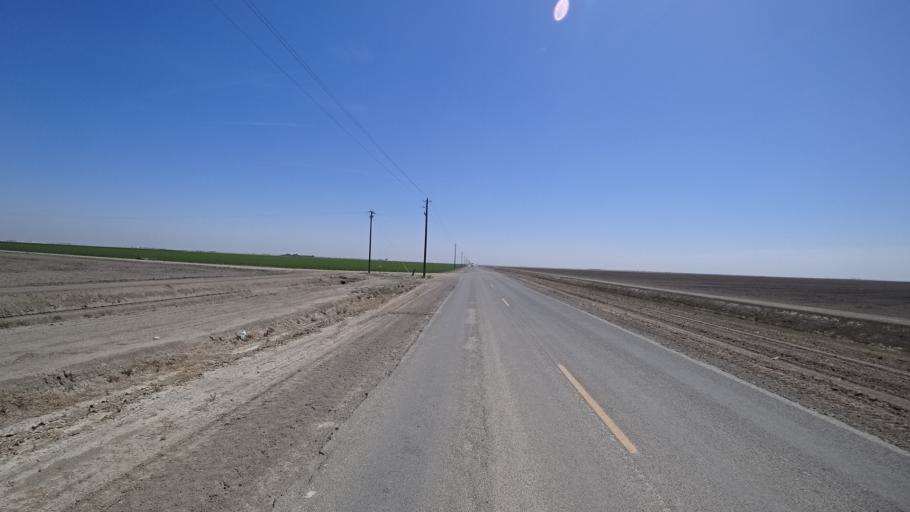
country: US
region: California
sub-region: Kings County
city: Corcoran
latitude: 36.0215
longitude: -119.5996
